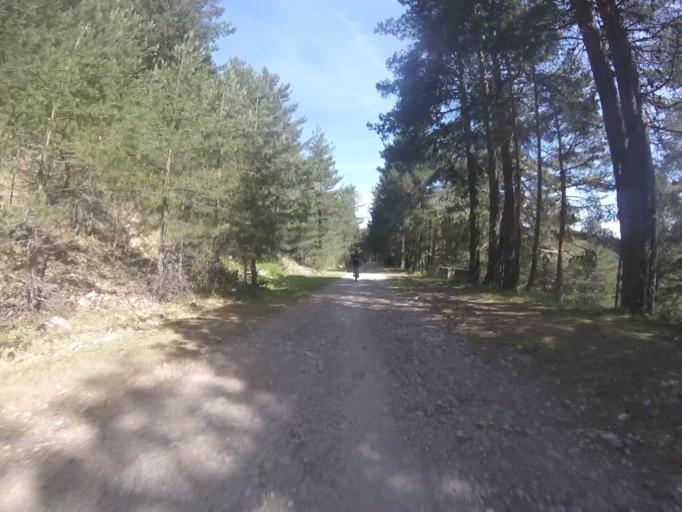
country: ES
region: Madrid
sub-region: Provincia de Madrid
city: Cercedilla
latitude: 40.8079
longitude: -4.0554
